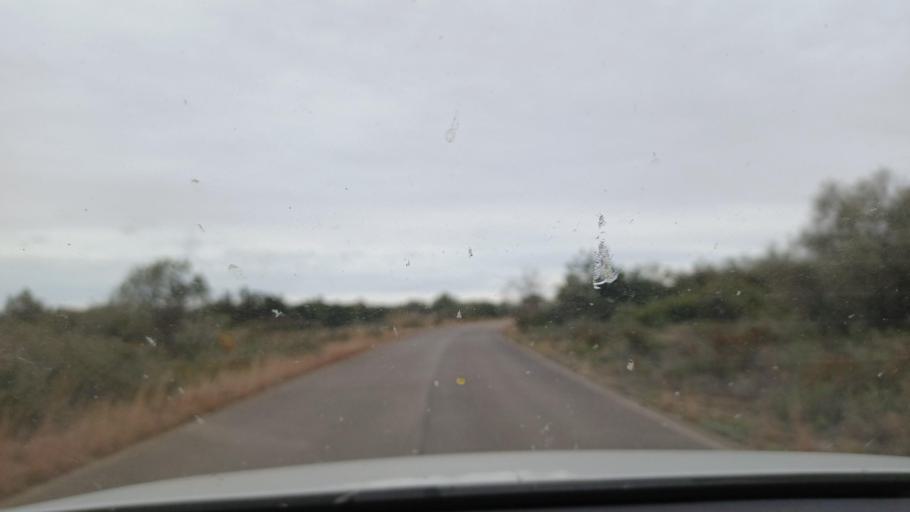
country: ES
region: Valencia
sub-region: Provincia de Castello
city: Canet lo Roig
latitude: 40.5875
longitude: 0.2845
